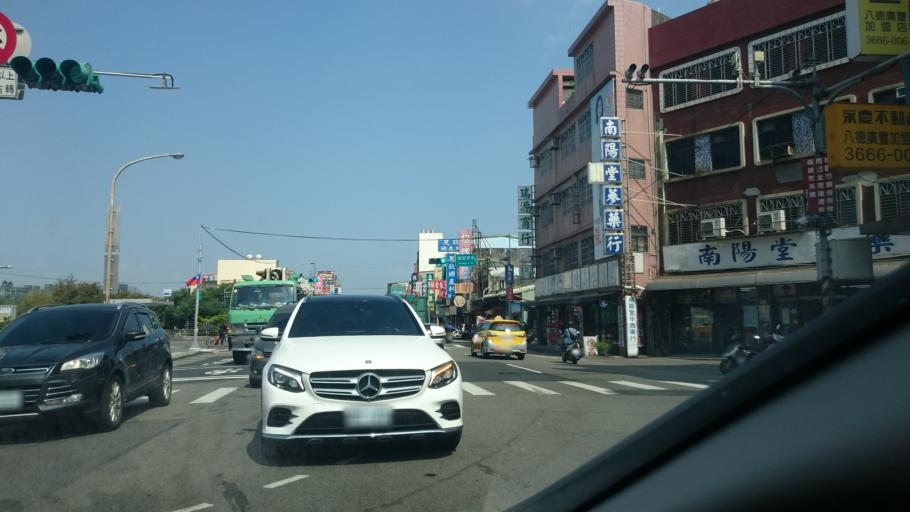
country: TW
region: Taiwan
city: Taoyuan City
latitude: 24.9642
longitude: 121.3004
